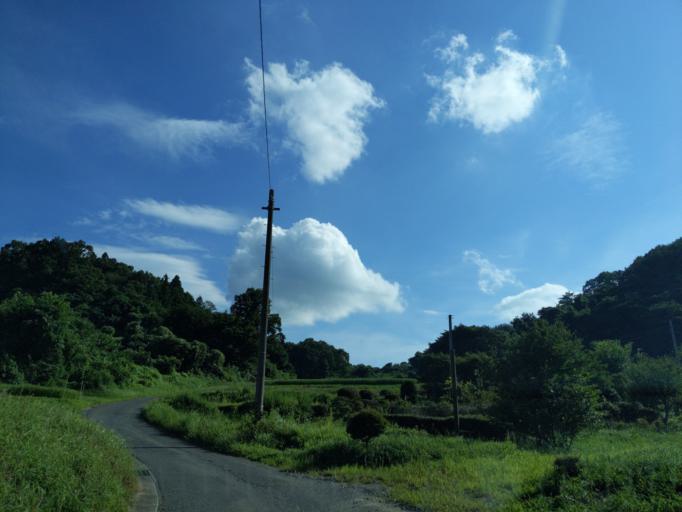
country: JP
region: Fukushima
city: Koriyama
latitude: 37.3979
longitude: 140.4278
